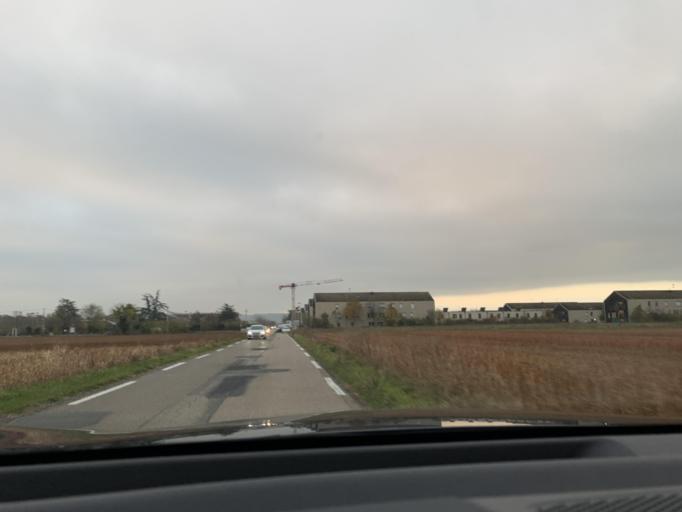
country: FR
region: Rhone-Alpes
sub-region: Departement du Rhone
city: Corbas
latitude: 45.6664
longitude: 4.9117
